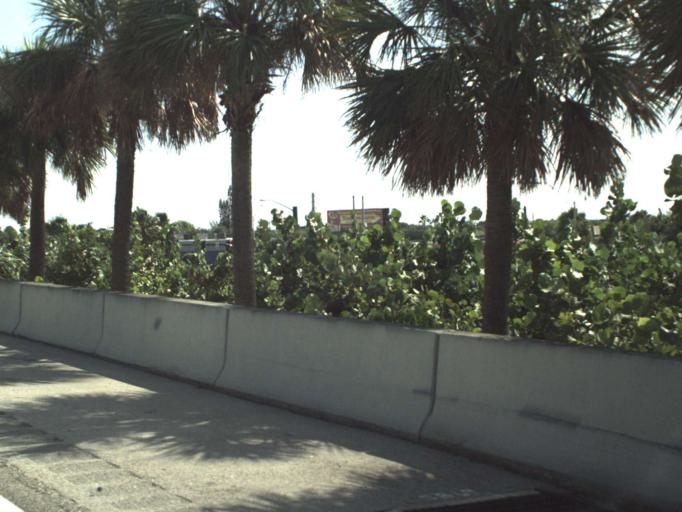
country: US
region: Florida
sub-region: Palm Beach County
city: North Palm Beach
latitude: 26.8078
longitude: -80.0981
